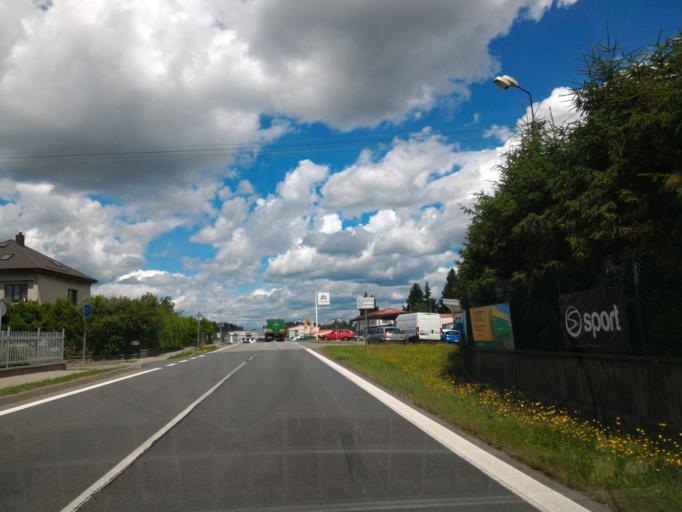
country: CZ
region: Vysocina
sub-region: Okres Zd'ar nad Sazavou
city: Nove Veseli
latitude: 49.5225
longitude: 15.9092
